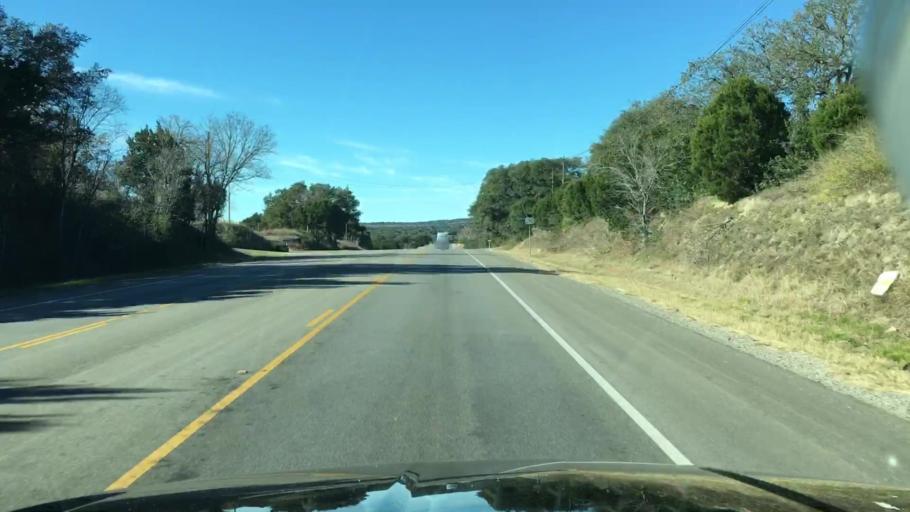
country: US
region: Texas
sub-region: Hays County
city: Dripping Springs
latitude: 30.1979
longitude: -98.2046
